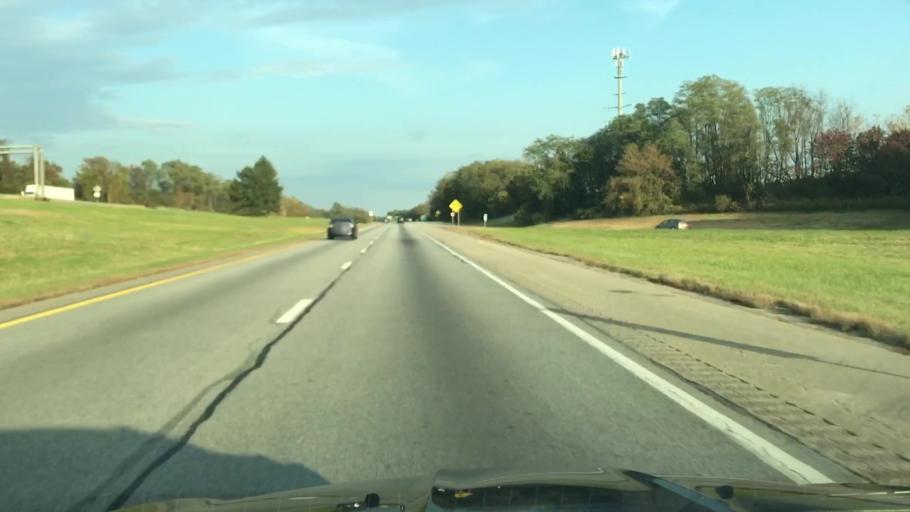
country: US
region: Pennsylvania
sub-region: Cumberland County
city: Mechanicsburg
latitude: 40.2748
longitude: -76.9989
